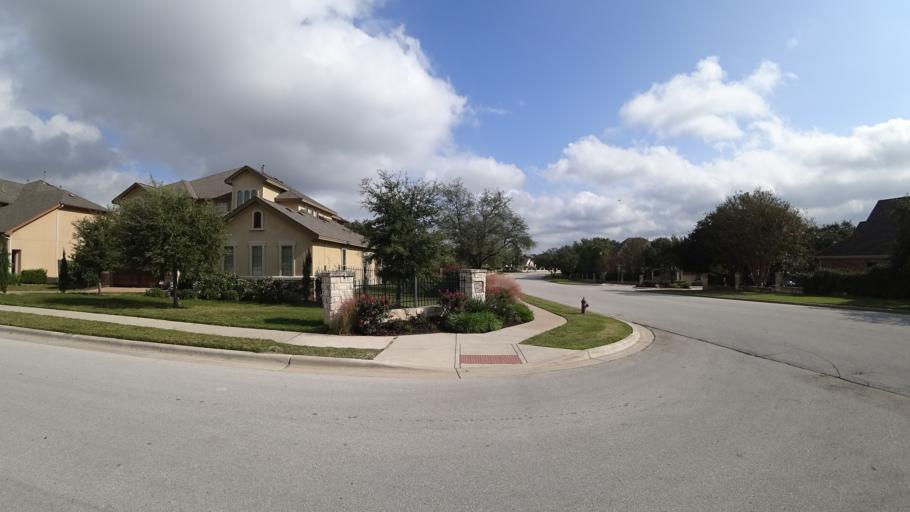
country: US
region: Texas
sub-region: Travis County
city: Barton Creek
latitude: 30.3121
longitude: -97.9012
